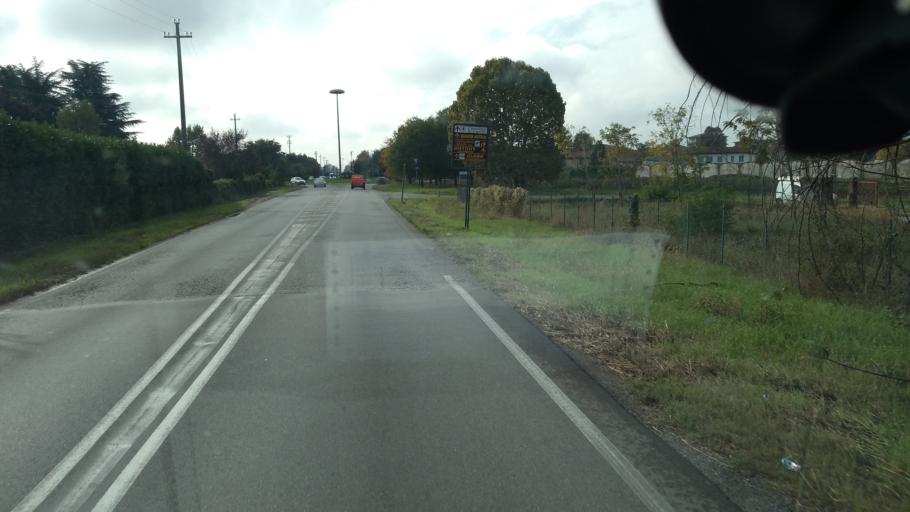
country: IT
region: Lombardy
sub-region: Provincia di Bergamo
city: Brignano Gera d'Adda
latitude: 45.5483
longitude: 9.6435
